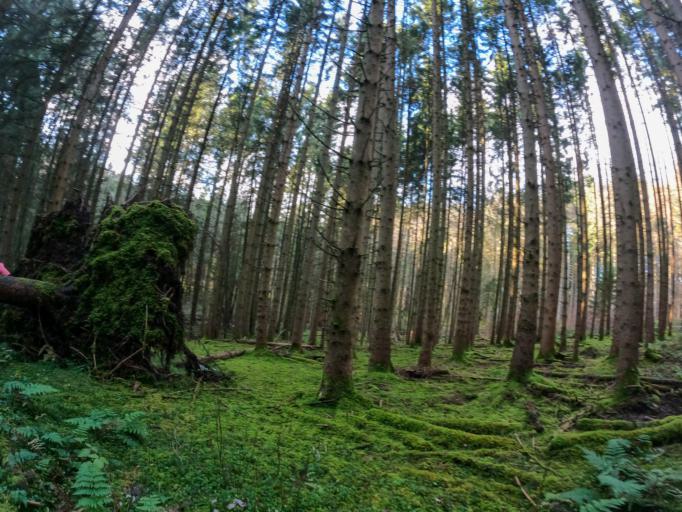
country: LU
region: Diekirch
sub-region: Canton de Wiltz
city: Bavigne
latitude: 49.9735
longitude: 5.8212
